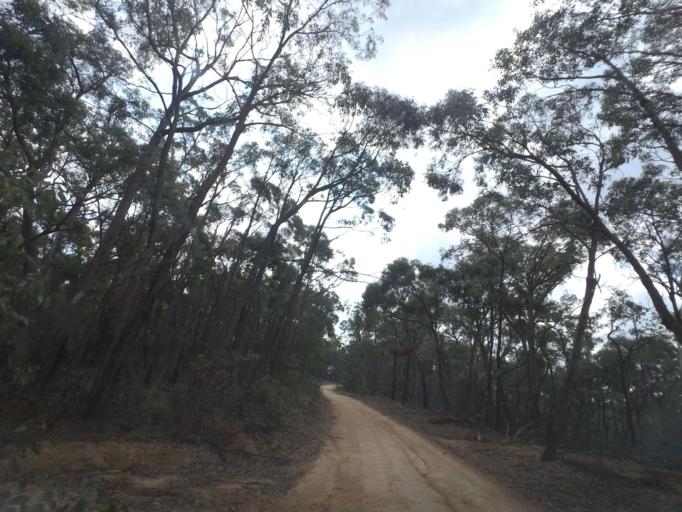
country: AU
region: Victoria
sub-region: Moorabool
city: Bacchus Marsh
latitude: -37.5104
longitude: 144.4308
